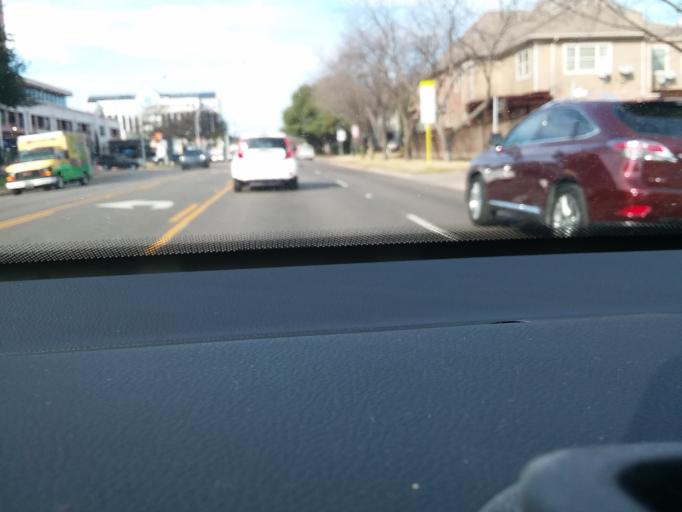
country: US
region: Texas
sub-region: Dallas County
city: University Park
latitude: 32.8600
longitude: -96.8042
